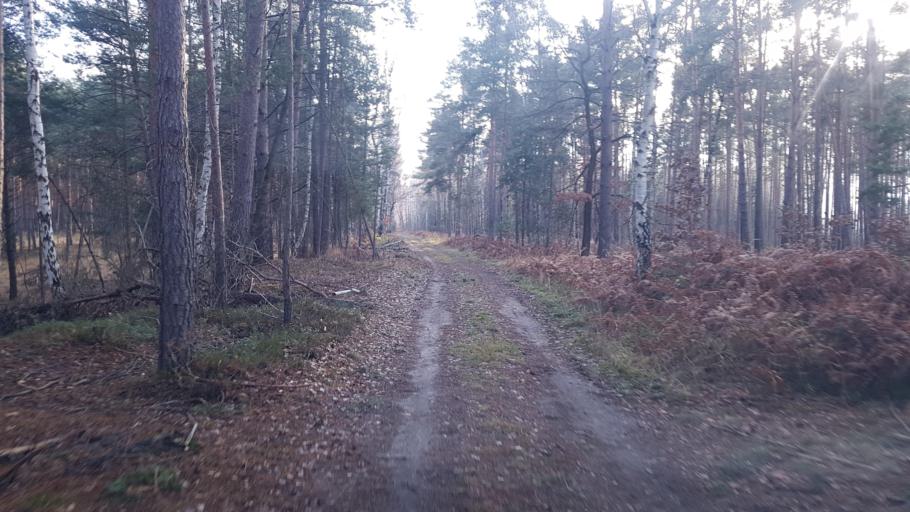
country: DE
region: Brandenburg
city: Plessa
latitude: 51.5251
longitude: 13.6819
